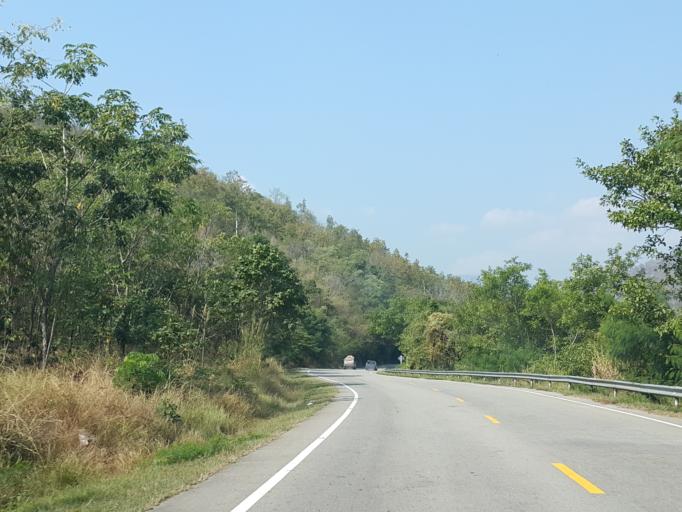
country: TH
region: Chiang Mai
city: Hot
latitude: 18.2214
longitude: 98.5744
